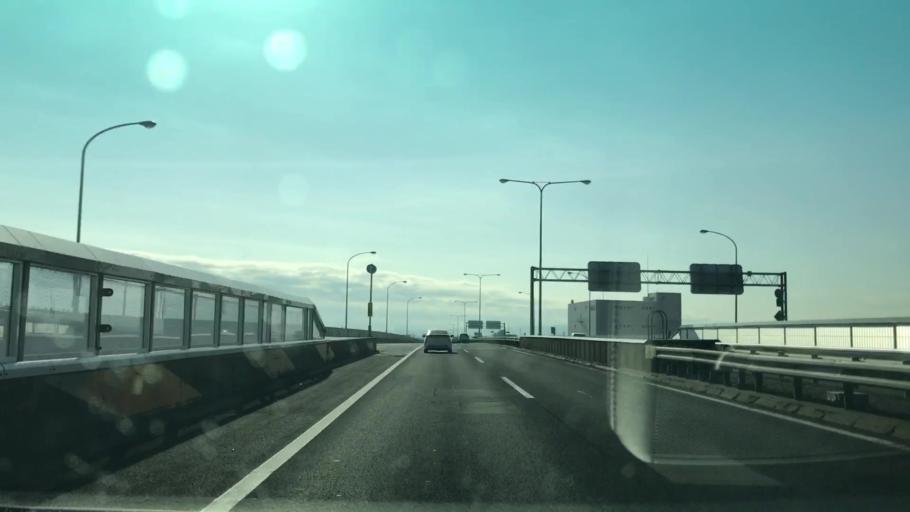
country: JP
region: Hokkaido
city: Sapporo
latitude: 43.0750
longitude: 141.4212
